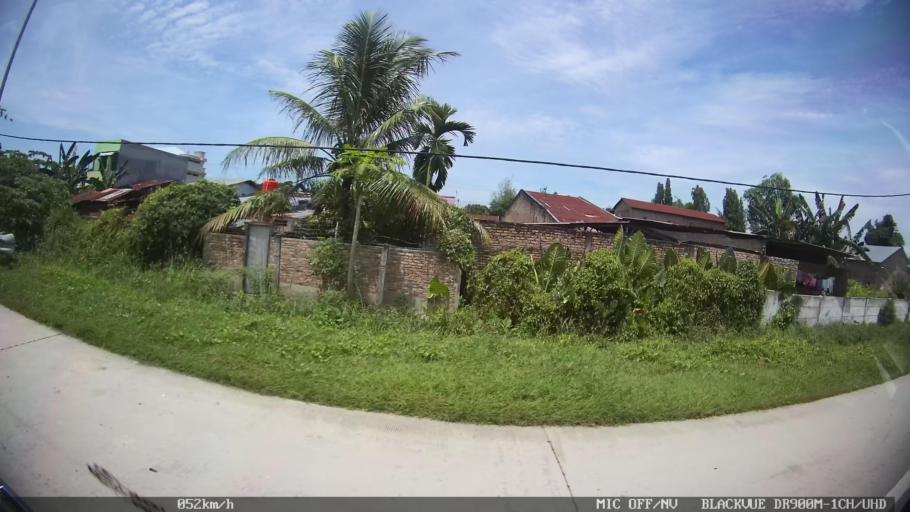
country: ID
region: North Sumatra
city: Perbaungan
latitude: 3.5546
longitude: 98.8866
